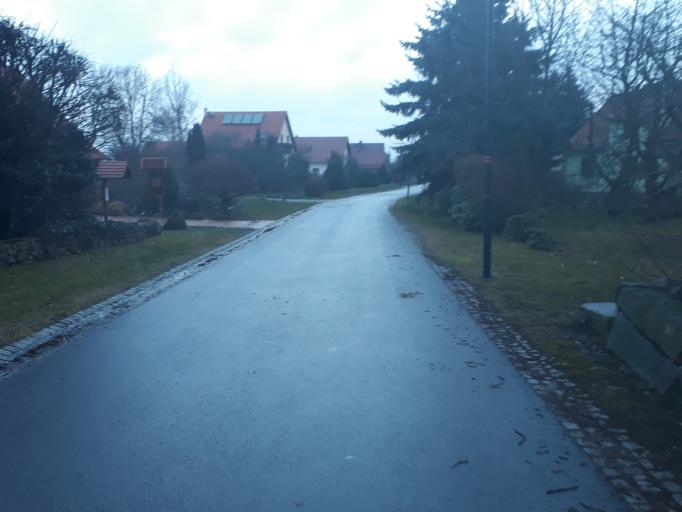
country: DE
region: Saxony
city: Guttau
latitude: 51.2597
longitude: 14.5513
